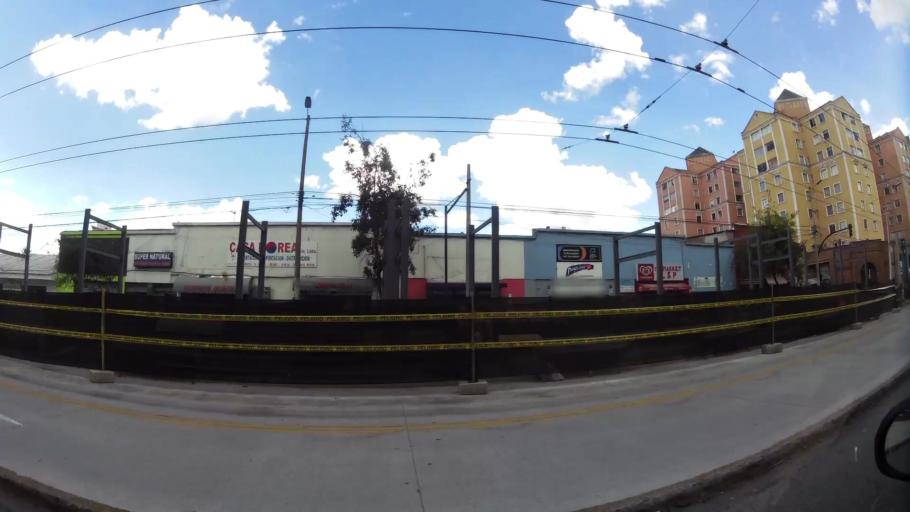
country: EC
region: Pichincha
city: Quito
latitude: -0.2043
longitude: -78.4987
